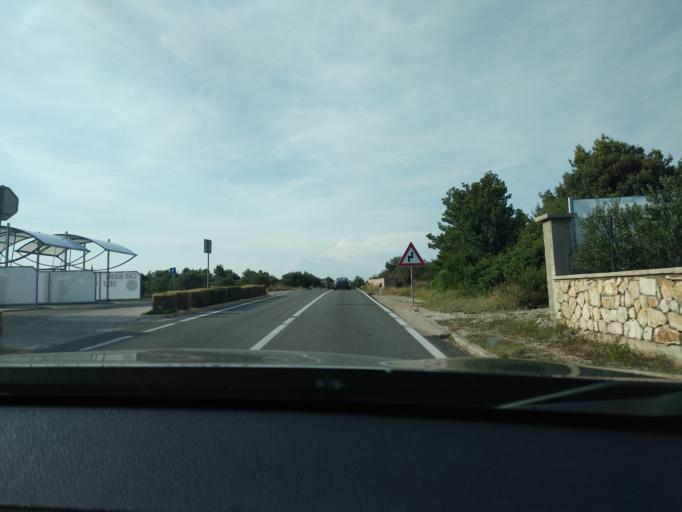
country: HR
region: Sibensko-Kniniska
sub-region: Grad Sibenik
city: Tisno
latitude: 43.7926
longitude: 15.6327
